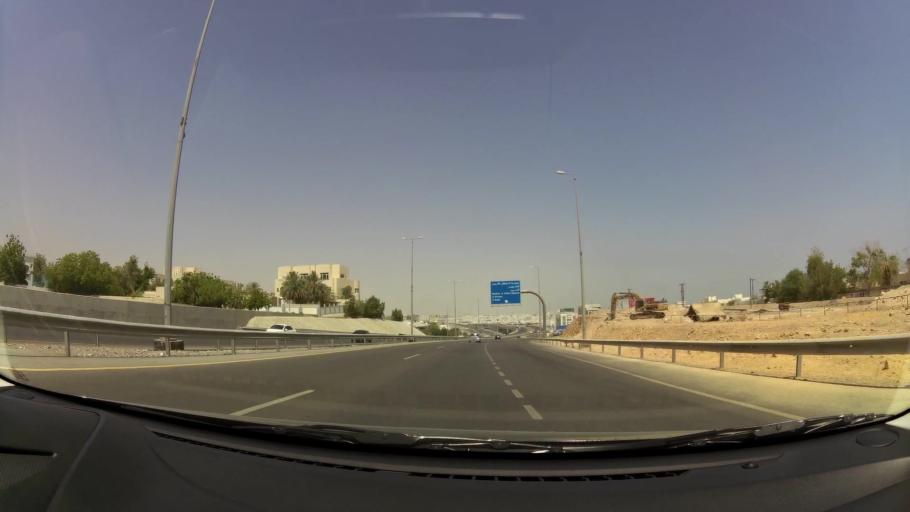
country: OM
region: Muhafazat Masqat
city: Bawshar
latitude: 23.5902
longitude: 58.4526
